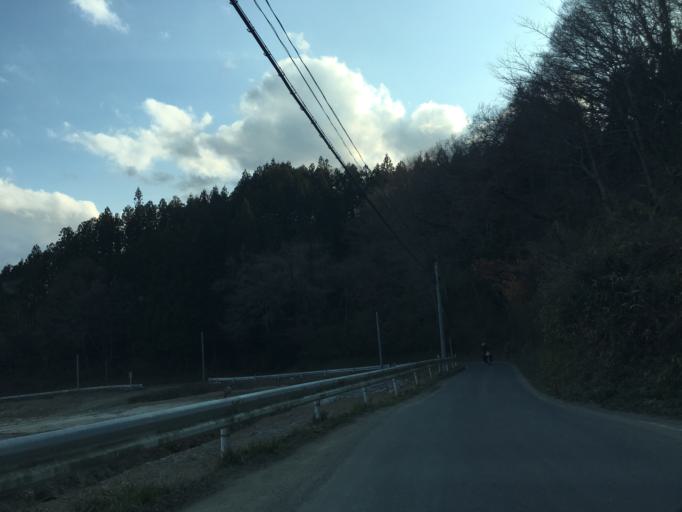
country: JP
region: Fukushima
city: Ishikawa
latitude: 37.1333
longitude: 140.5920
